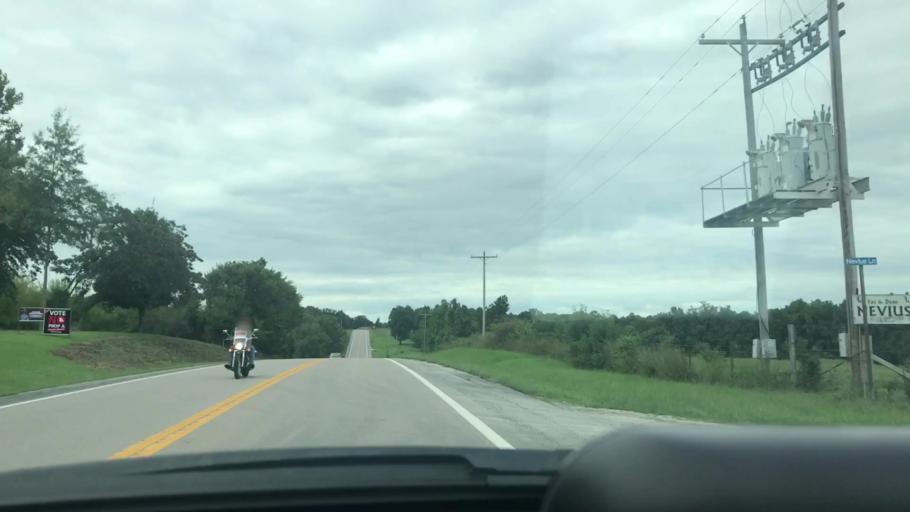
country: US
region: Missouri
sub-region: Benton County
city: Warsaw
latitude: 38.1485
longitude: -93.2925
